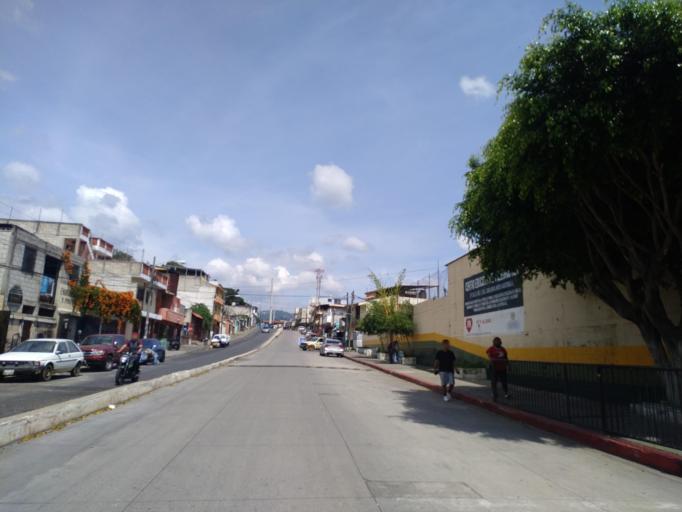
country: GT
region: Guatemala
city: Mixco
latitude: 14.6681
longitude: -90.5816
